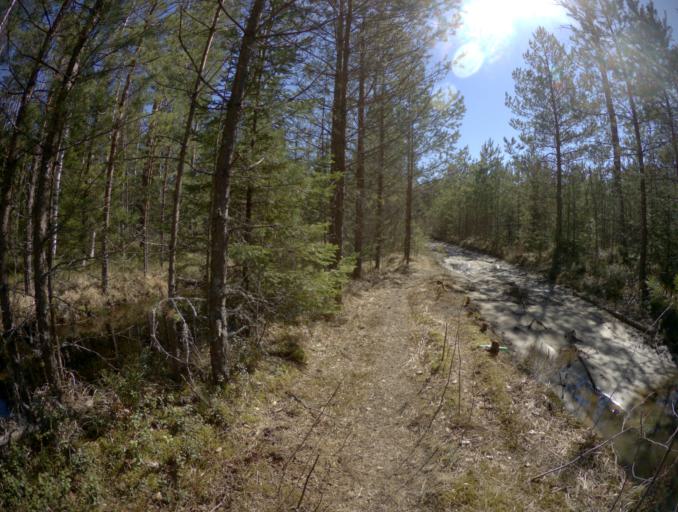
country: RU
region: Vladimir
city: Ivanishchi
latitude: 55.8164
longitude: 40.4188
